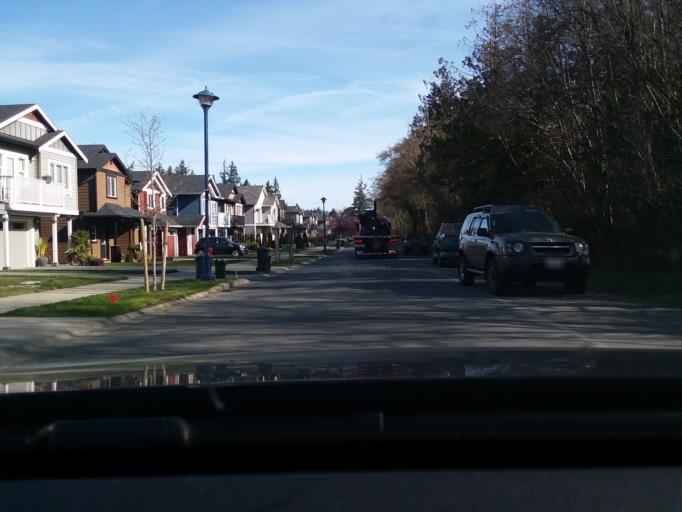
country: CA
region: British Columbia
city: Langford
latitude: 48.4258
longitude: -123.5328
